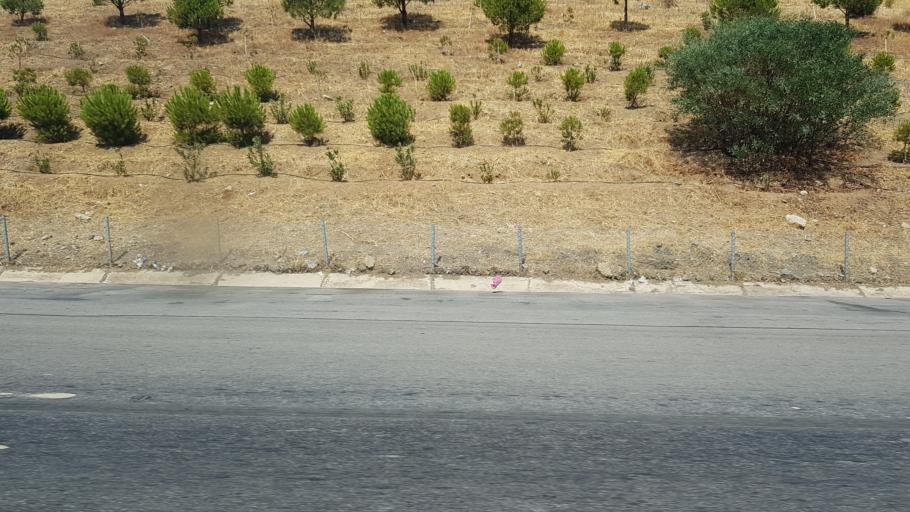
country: TR
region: Izmir
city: Urla
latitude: 38.3761
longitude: 26.9300
